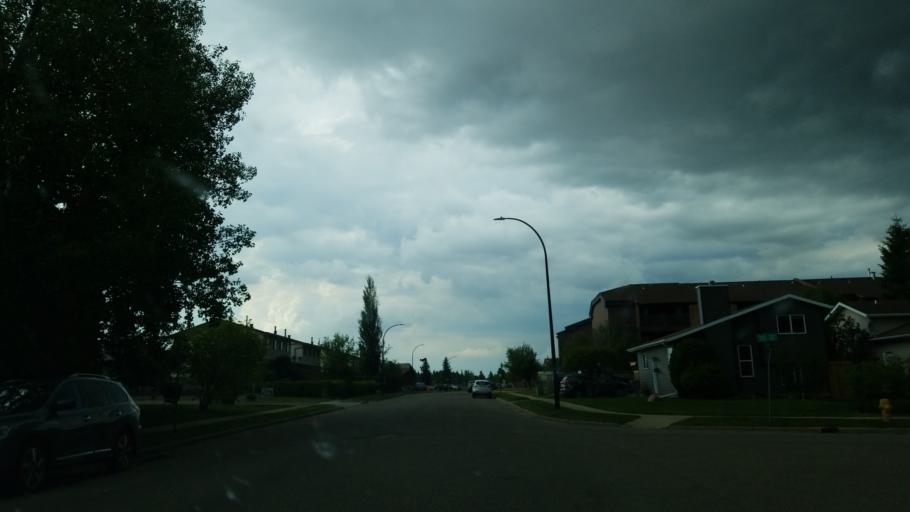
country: CA
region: Saskatchewan
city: Lloydminster
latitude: 53.2650
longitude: -110.0214
